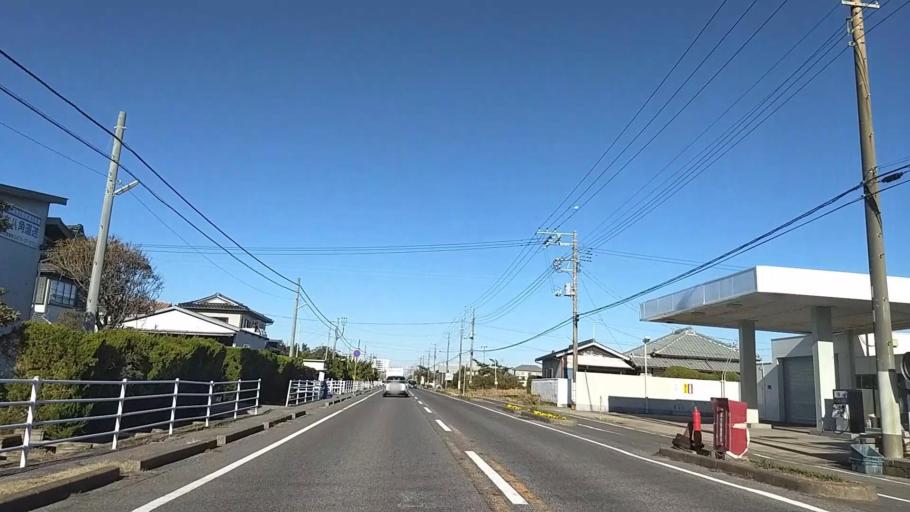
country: JP
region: Chiba
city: Togane
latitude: 35.4791
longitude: 140.4166
